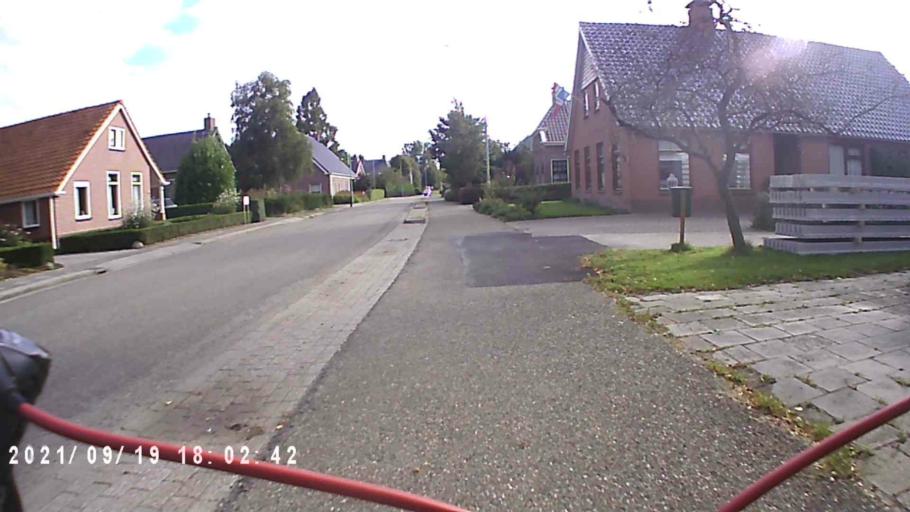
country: NL
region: Groningen
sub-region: Gemeente Delfzijl
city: Delfzijl
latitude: 53.2495
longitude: 6.9277
